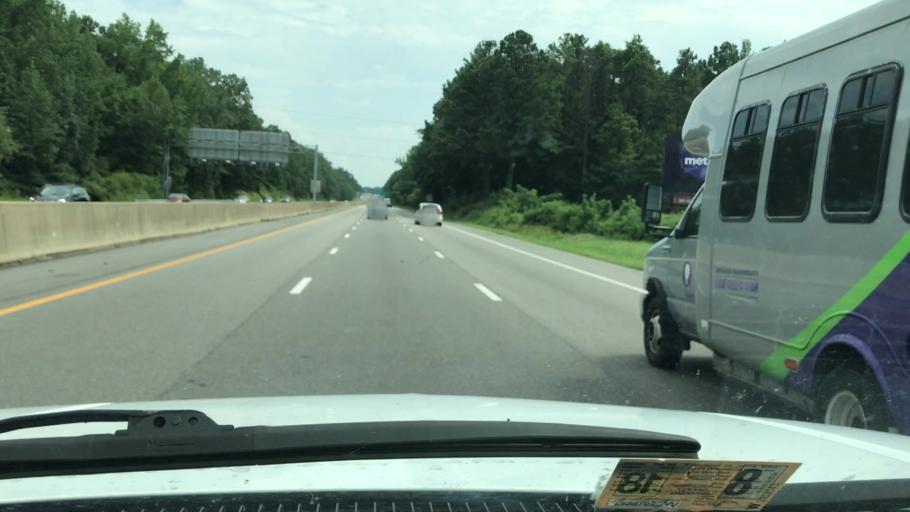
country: US
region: Virginia
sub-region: Chesterfield County
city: Bon Air
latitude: 37.4959
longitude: -77.5227
